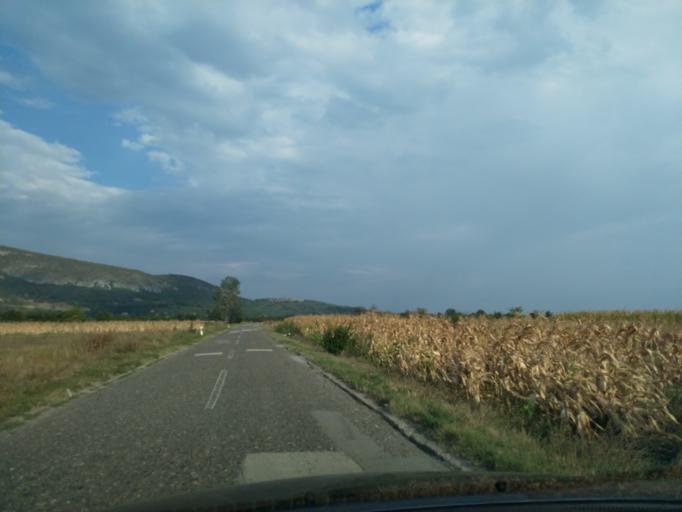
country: RS
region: Central Serbia
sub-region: Pomoravski Okrug
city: Paracin
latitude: 43.8245
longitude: 21.5287
